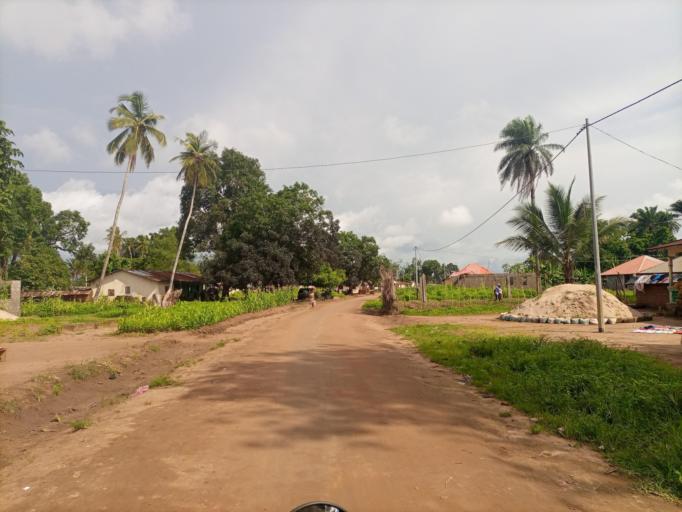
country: SL
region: Northern Province
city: Masoyila
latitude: 8.6142
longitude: -13.1713
